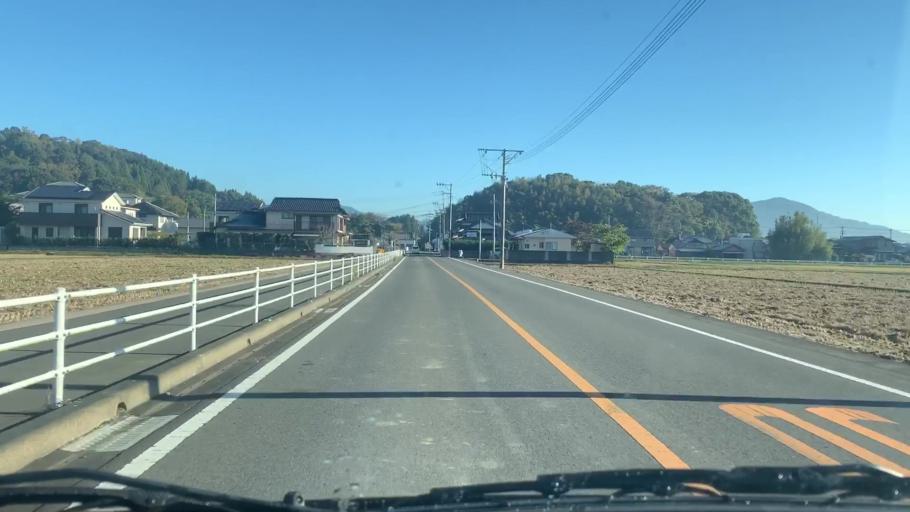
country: JP
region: Saga Prefecture
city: Takeocho-takeo
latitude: 33.2118
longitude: 130.0378
